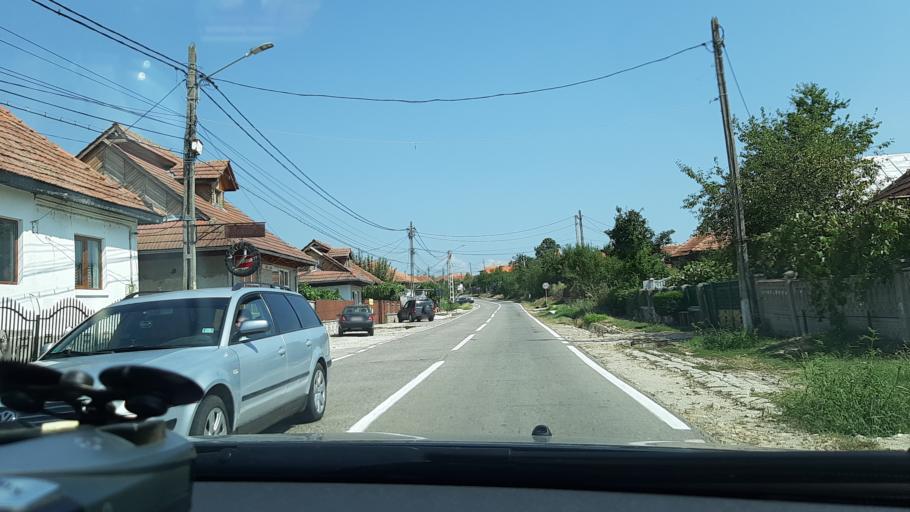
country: RO
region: Gorj
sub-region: Comuna Targu Carbunesti
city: Targu Carbunesti
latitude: 44.9436
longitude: 23.5358
